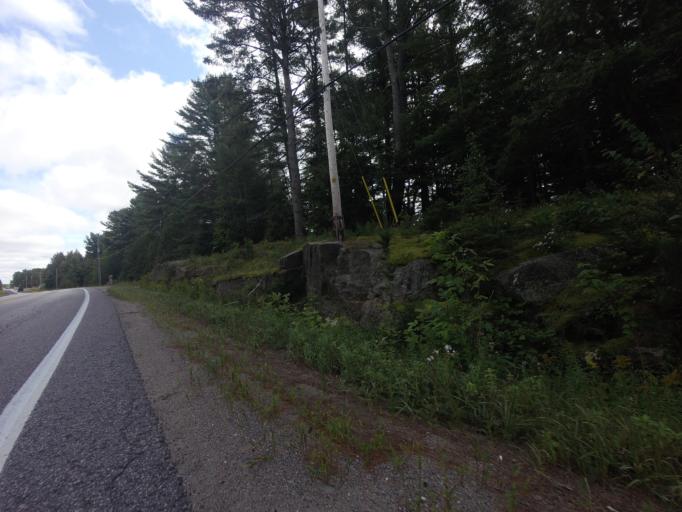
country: CA
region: Ontario
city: Omemee
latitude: 44.8024
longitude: -78.6194
